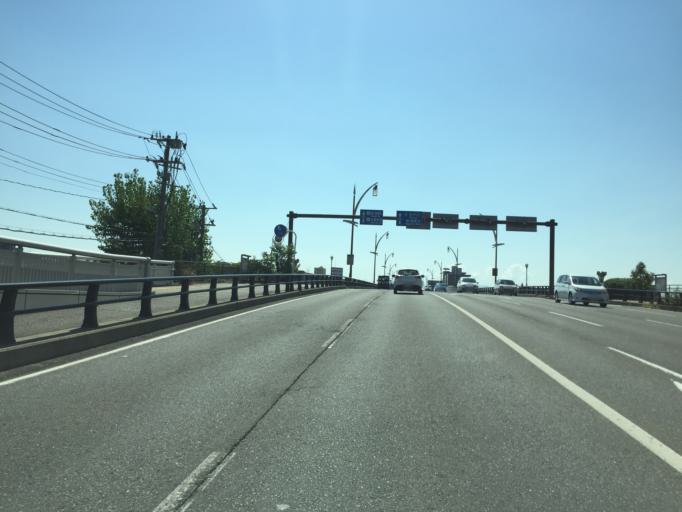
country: JP
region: Niigata
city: Niigata-shi
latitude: 37.9137
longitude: 139.0422
